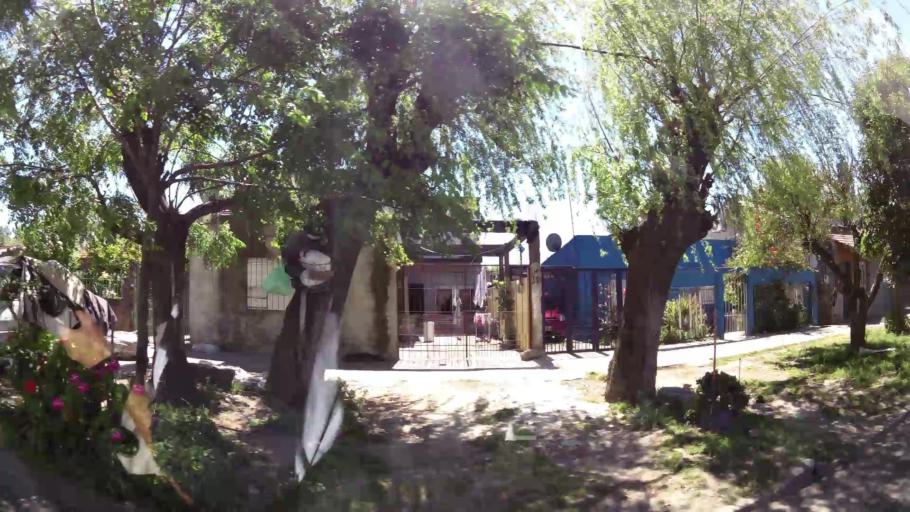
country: AR
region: Buenos Aires
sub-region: Partido de Lanus
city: Lanus
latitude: -34.7277
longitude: -58.3342
